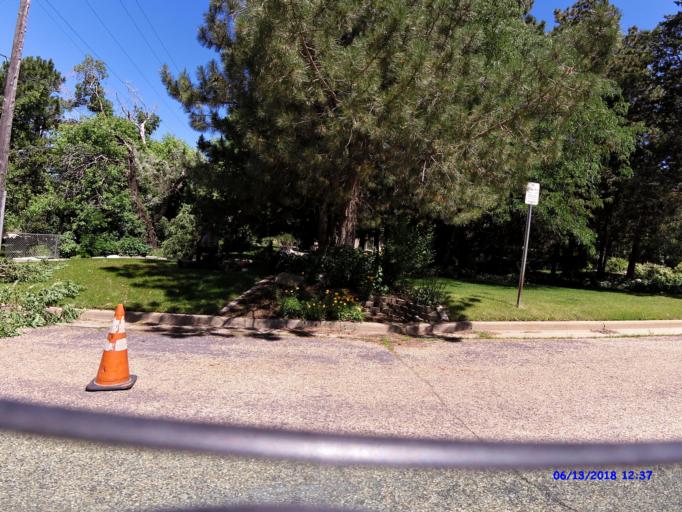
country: US
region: Utah
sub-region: Weber County
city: South Ogden
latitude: 41.1986
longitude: -111.9392
